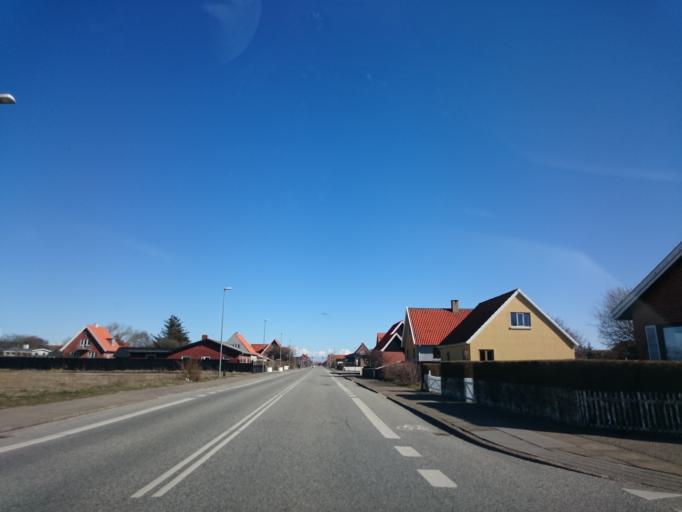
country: DK
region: North Denmark
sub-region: Frederikshavn Kommune
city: Skagen
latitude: 57.7272
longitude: 10.5800
